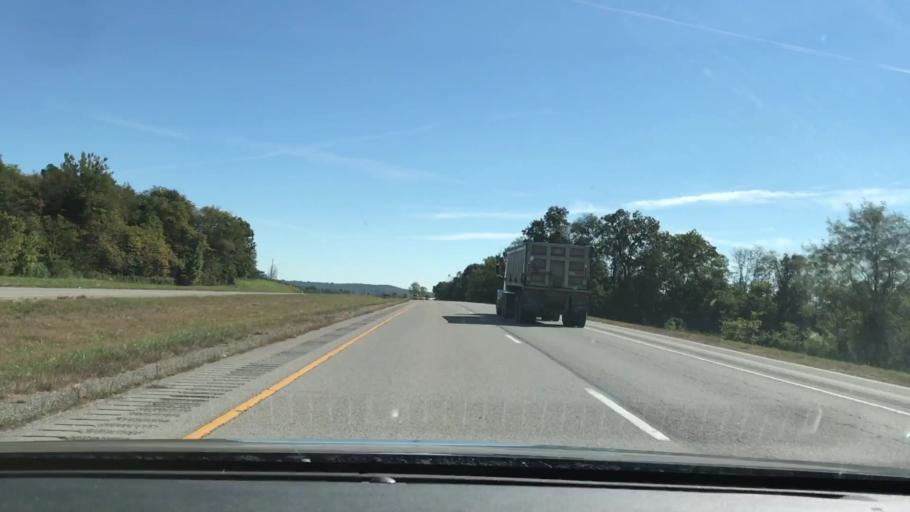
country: US
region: Kentucky
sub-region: Todd County
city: Elkton
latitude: 36.8460
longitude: -87.2927
